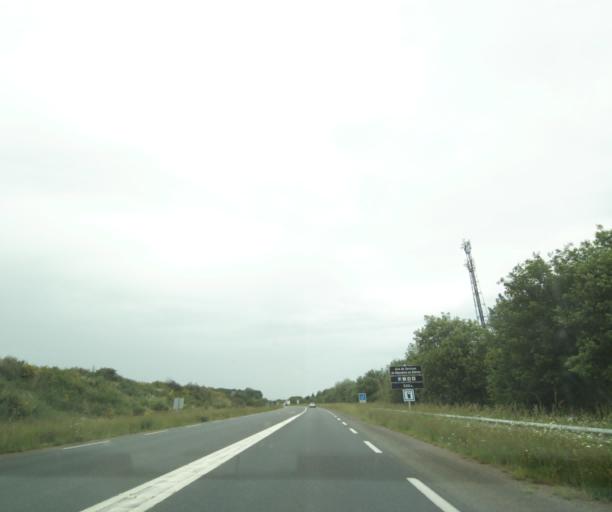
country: FR
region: Poitou-Charentes
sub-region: Departement des Deux-Sevres
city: Saint-Pardoux
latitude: 46.5402
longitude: -0.3138
